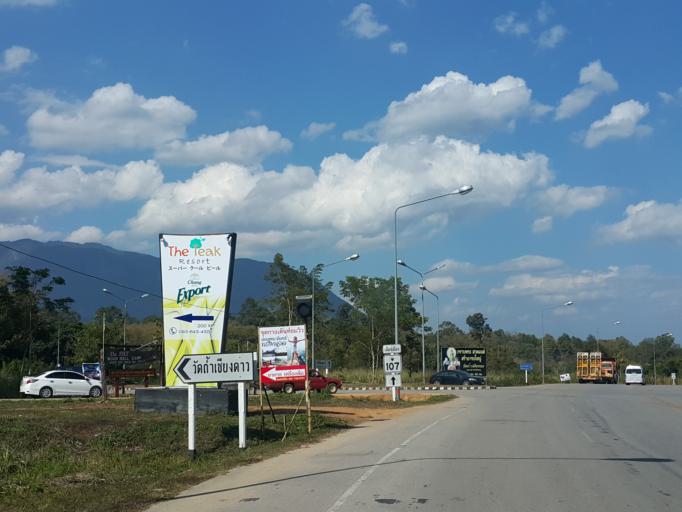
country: TH
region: Chiang Mai
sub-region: Amphoe Chiang Dao
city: Chiang Dao
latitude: 19.3765
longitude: 98.9462
